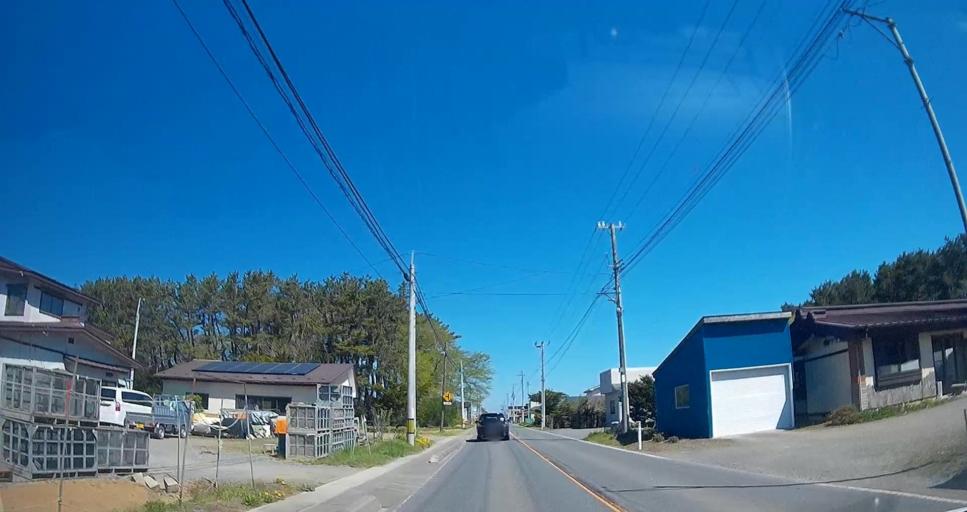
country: JP
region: Aomori
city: Misawa
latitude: 40.6778
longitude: 141.4293
